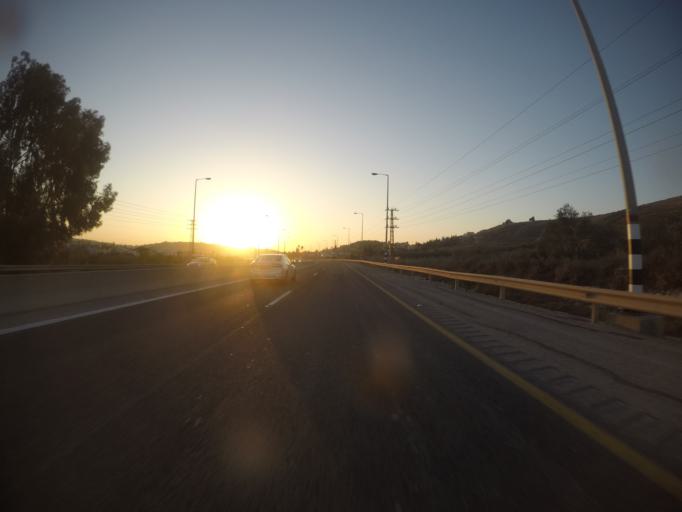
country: PS
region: West Bank
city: Barta`ah ash Sharqiyah
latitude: 32.5056
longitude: 35.0919
